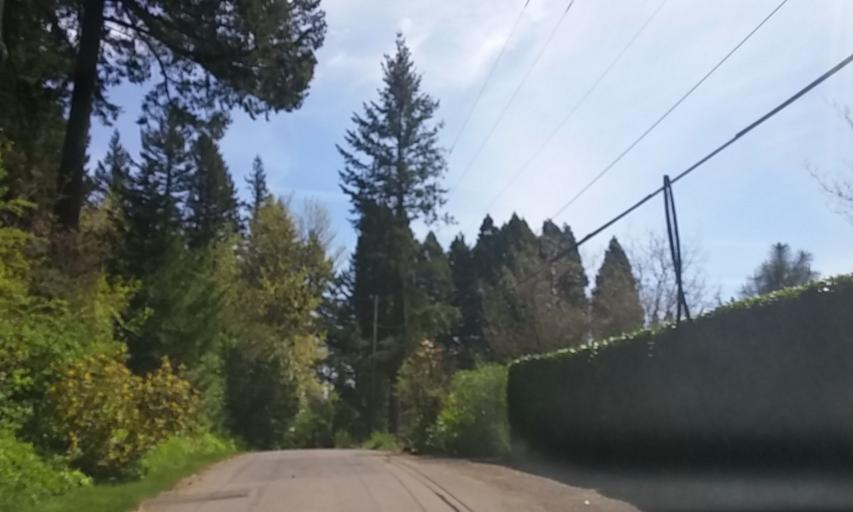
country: US
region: Oregon
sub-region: Washington County
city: West Slope
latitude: 45.5108
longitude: -122.7397
